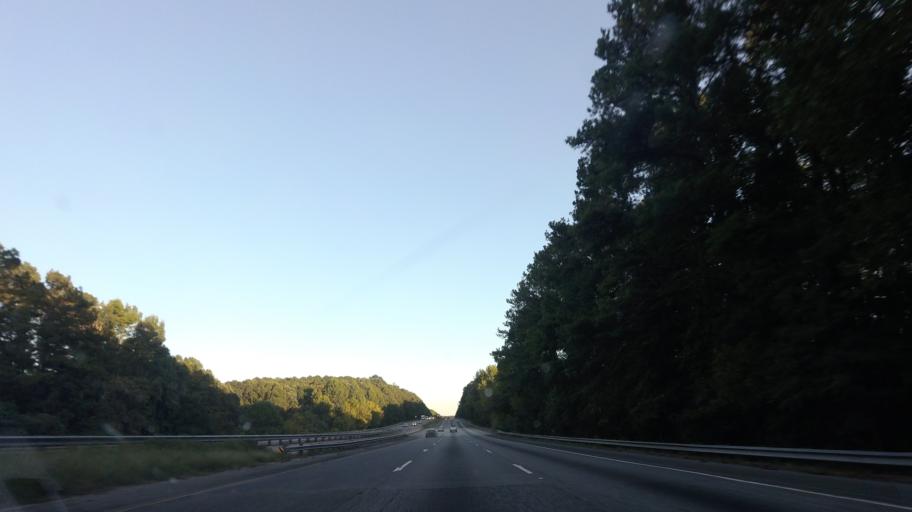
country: US
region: Georgia
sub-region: Monroe County
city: Forsyth
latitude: 33.1368
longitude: -84.0199
